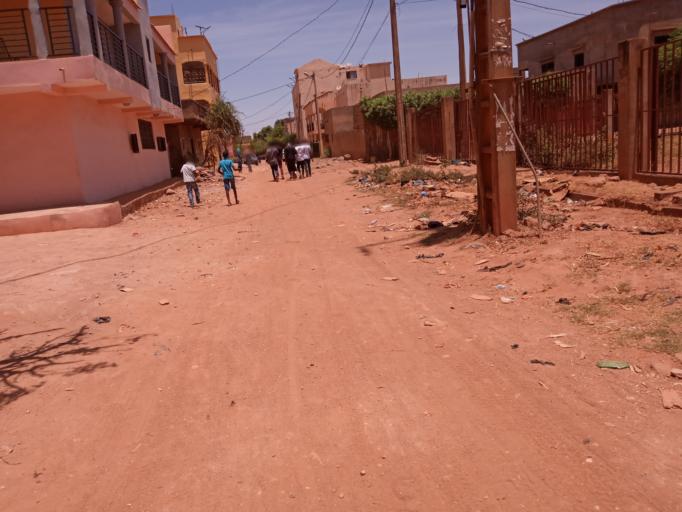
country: ML
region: Bamako
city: Bamako
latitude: 12.5856
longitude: -7.9543
